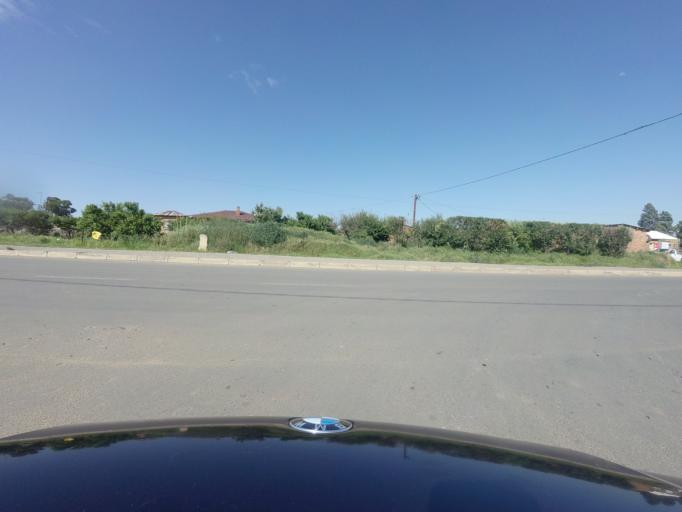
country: LS
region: Maseru
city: Maseru
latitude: -29.3067
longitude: 27.4945
